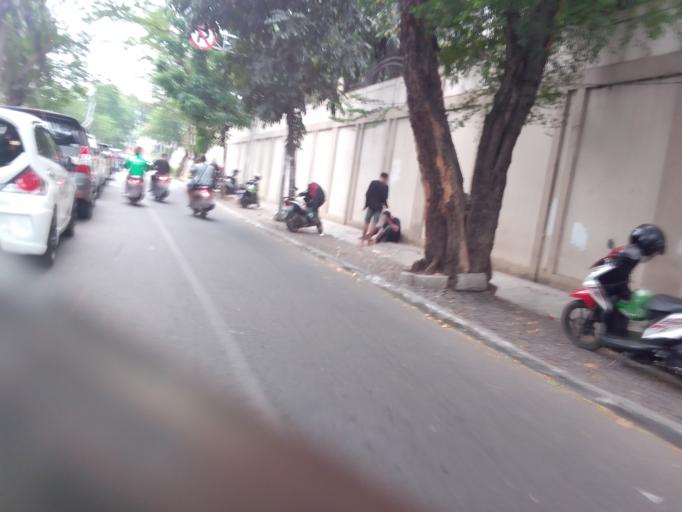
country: ID
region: Jakarta Raya
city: Jakarta
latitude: -6.1952
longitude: 106.8180
